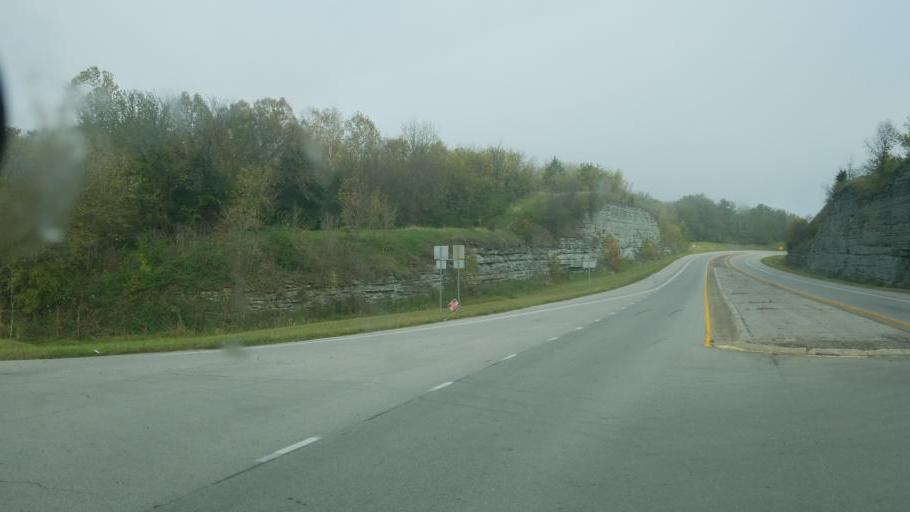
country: US
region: Kentucky
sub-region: Mason County
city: Maysville
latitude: 38.5490
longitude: -83.7630
